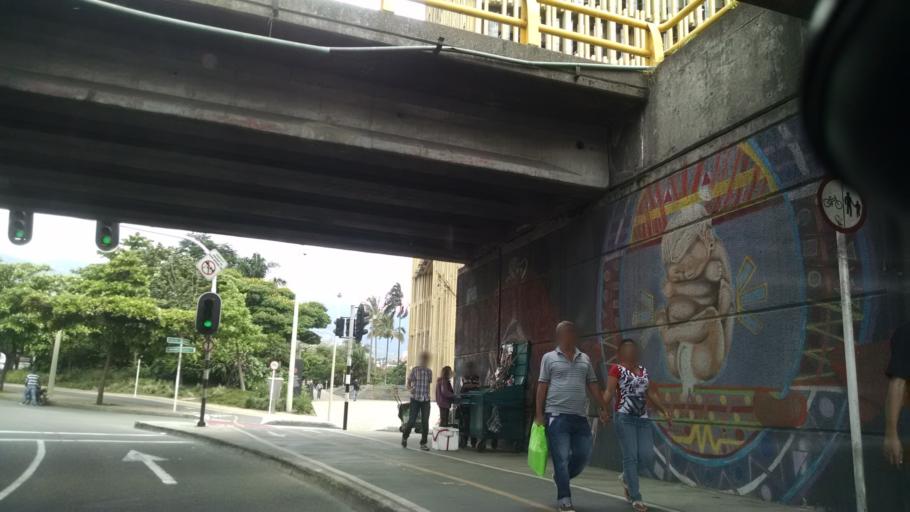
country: CO
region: Antioquia
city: Medellin
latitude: 6.2457
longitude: -75.5753
